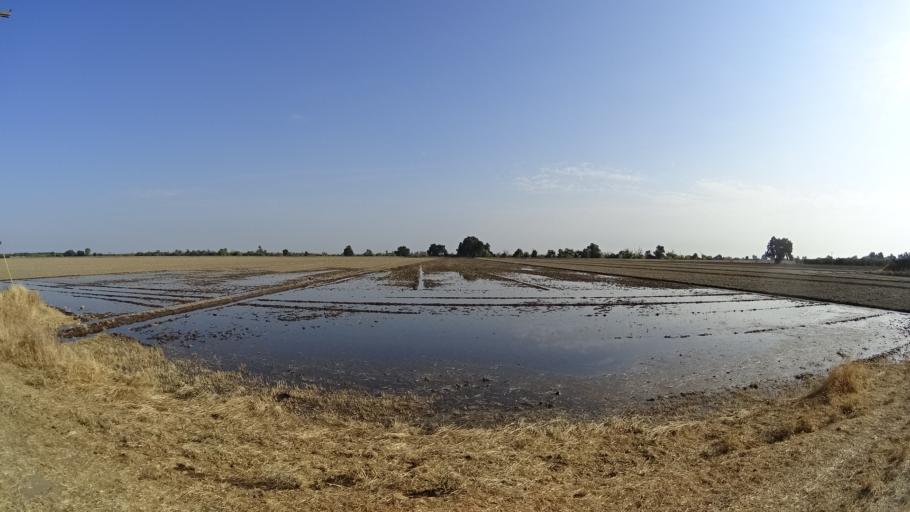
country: US
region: California
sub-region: Kings County
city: Lemoore
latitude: 36.3803
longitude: -119.7967
